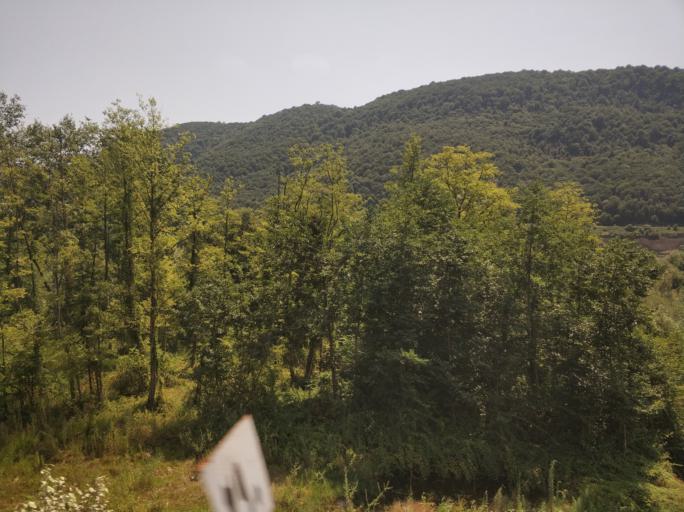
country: IR
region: Gilan
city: Pa'in-e Bazar-e Rudbar
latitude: 36.9840
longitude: 49.5579
